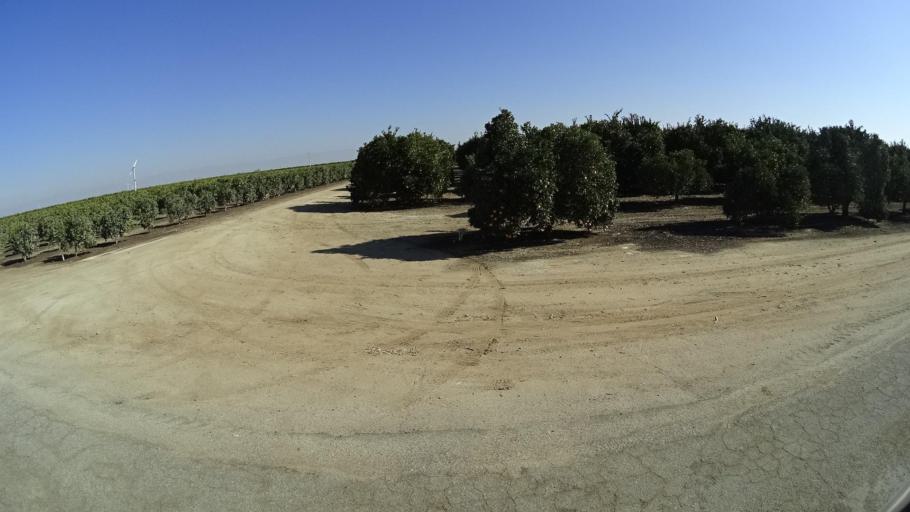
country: US
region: California
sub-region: Tulare County
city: Richgrove
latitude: 35.7198
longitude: -119.1428
